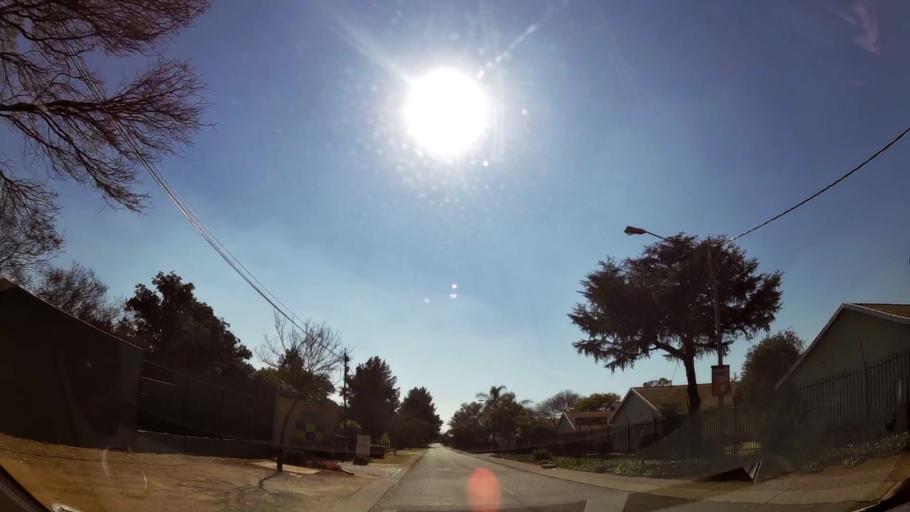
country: ZA
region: Gauteng
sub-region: City of Tshwane Metropolitan Municipality
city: Centurion
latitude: -25.8328
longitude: 28.1862
